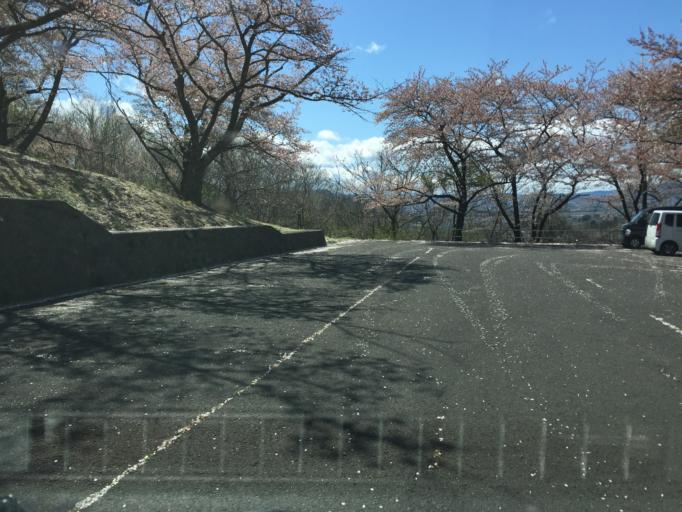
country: JP
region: Fukushima
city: Fukushima-shi
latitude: 37.8310
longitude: 140.4337
